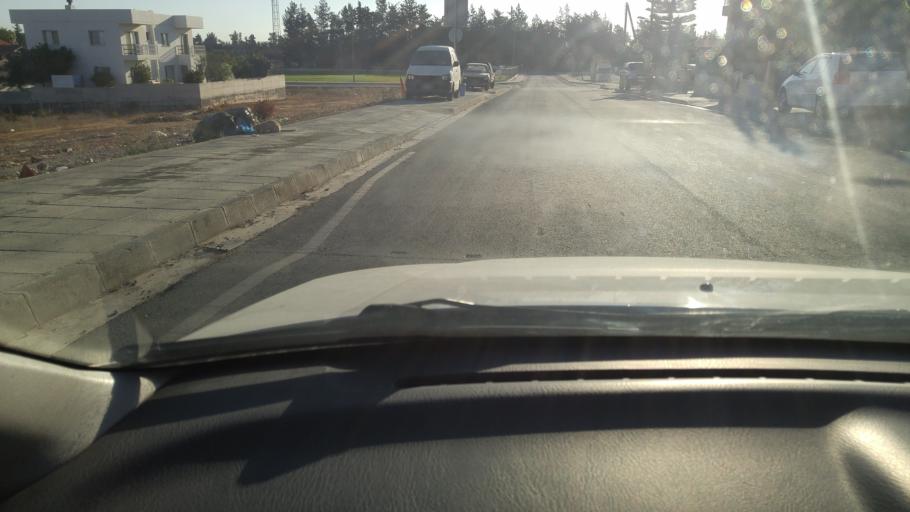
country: CY
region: Limassol
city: Ypsonas
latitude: 34.6607
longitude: 32.9688
